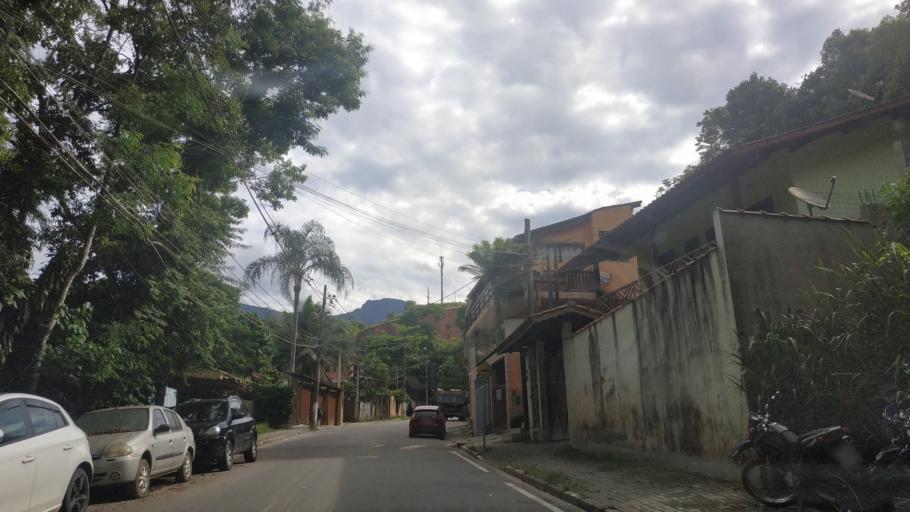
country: BR
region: Sao Paulo
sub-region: Ilhabela
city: Ilhabela
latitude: -23.8228
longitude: -45.3532
